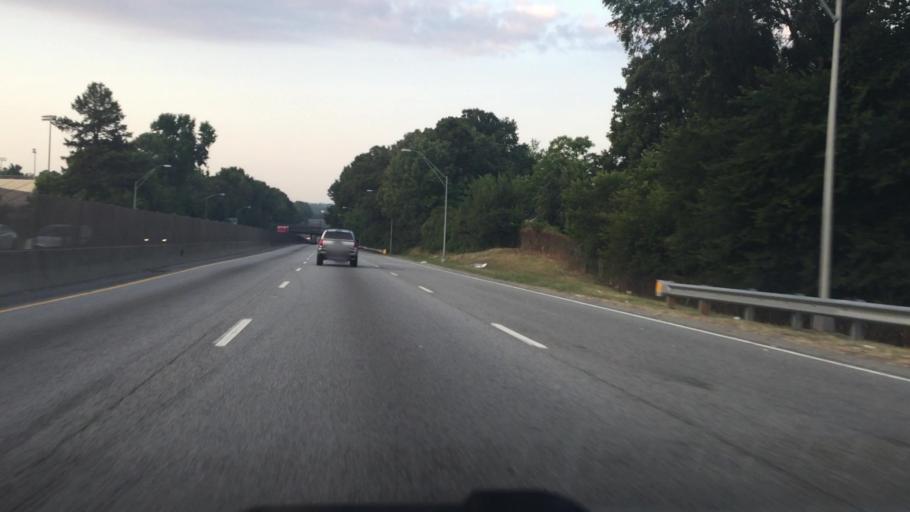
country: US
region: North Carolina
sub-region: Guilford County
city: Greensboro
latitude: 36.0613
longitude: -79.7678
